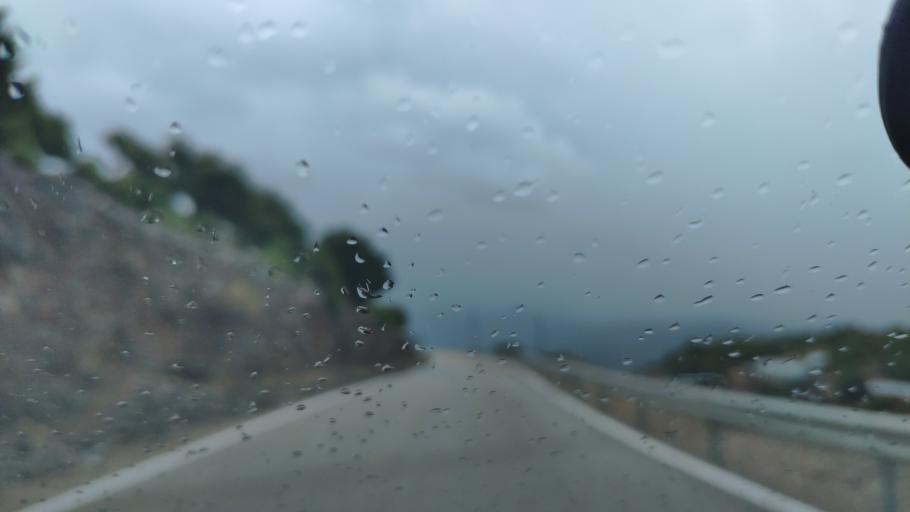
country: GR
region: Central Greece
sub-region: Nomos Evrytanias
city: Kerasochori
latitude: 39.0800
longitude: 21.3991
